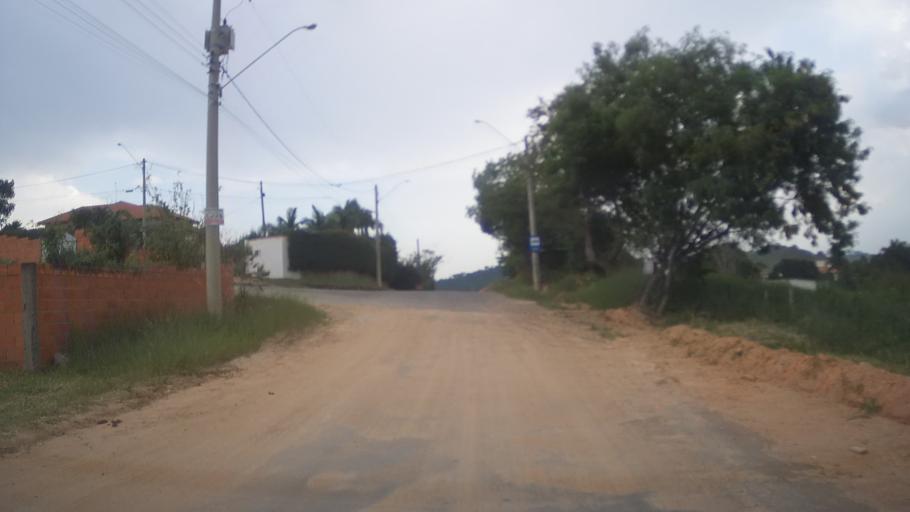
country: BR
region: Sao Paulo
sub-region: Itupeva
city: Itupeva
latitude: -23.1883
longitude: -47.0879
